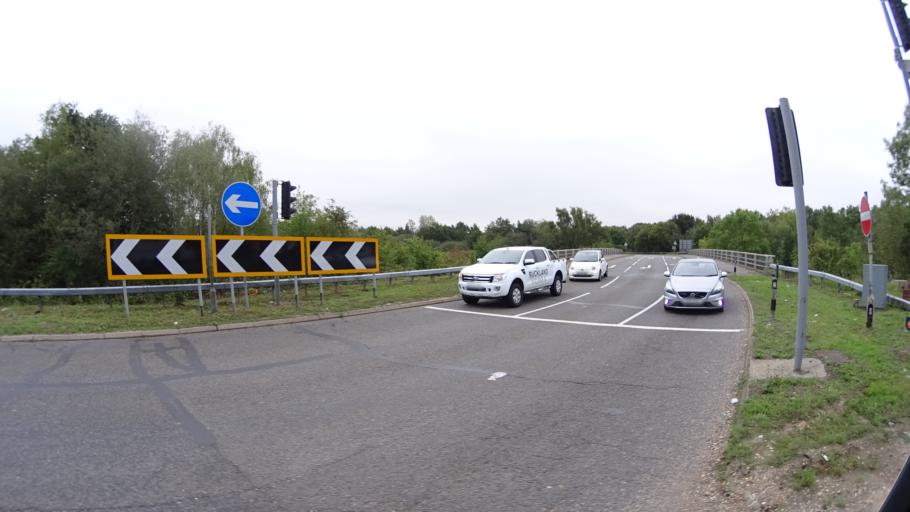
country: GB
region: England
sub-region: Hampshire
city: Hook
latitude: 51.2714
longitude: -0.9617
